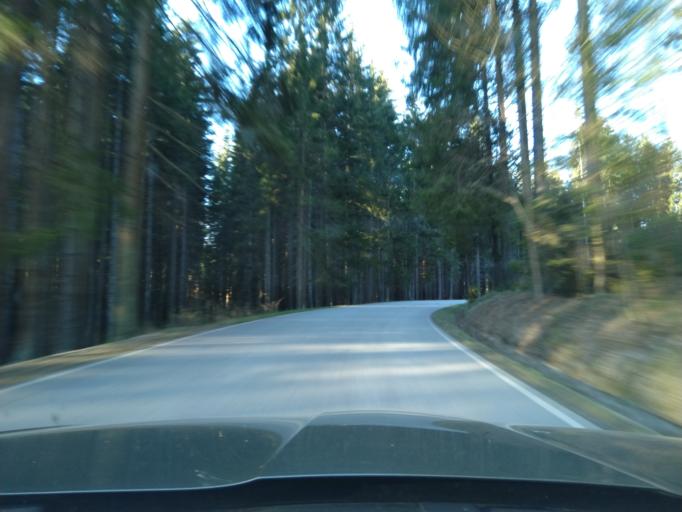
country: CZ
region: Jihocesky
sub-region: Okres Prachatice
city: Volary
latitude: 48.9036
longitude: 13.8214
